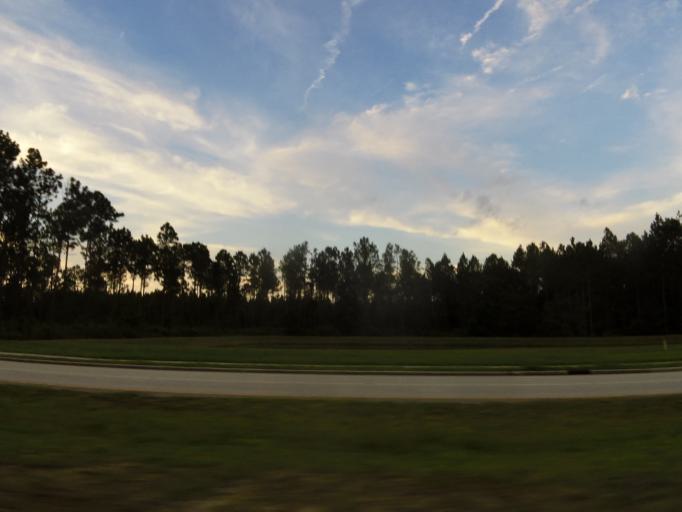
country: US
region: Florida
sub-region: Saint Johns County
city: Fruit Cove
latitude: 30.0823
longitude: -81.5633
